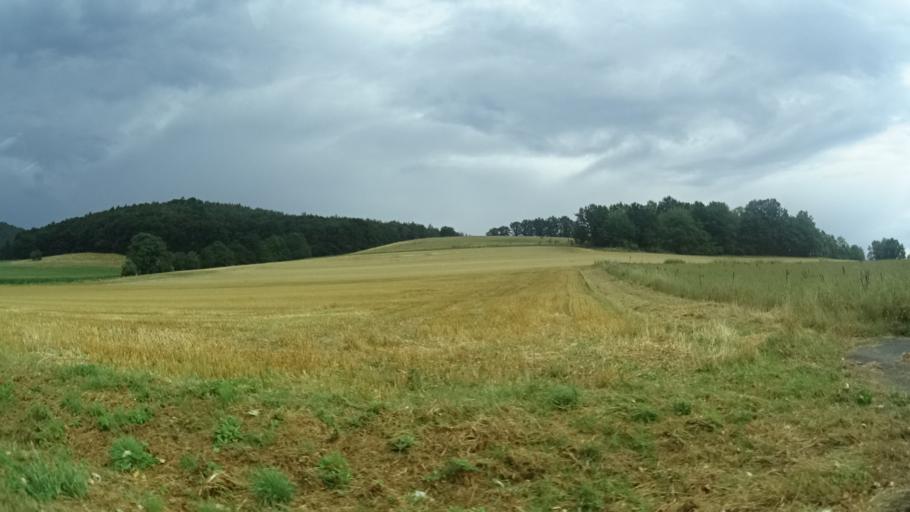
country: DE
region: Hesse
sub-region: Regierungsbezirk Kassel
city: Bad Hersfeld
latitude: 50.8214
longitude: 9.6728
